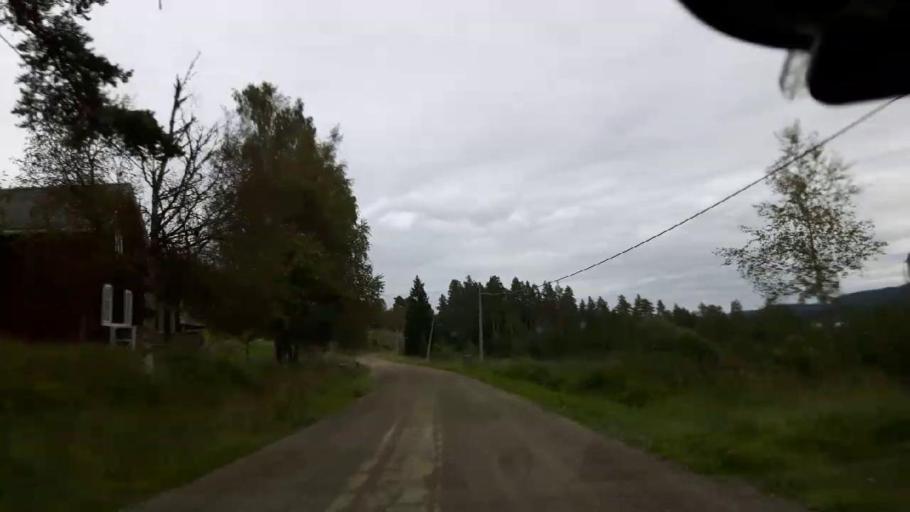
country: SE
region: Jaemtland
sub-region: Braecke Kommun
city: Braecke
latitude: 63.0396
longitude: 15.3602
